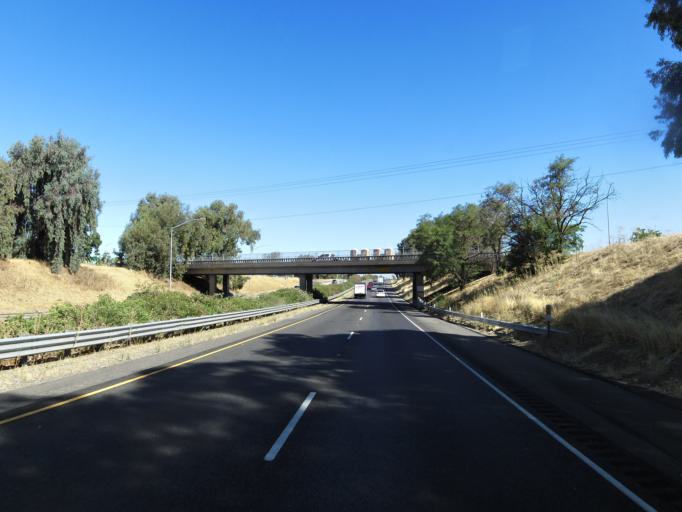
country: US
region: California
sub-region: Sacramento County
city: Galt
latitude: 38.2904
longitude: -121.3117
